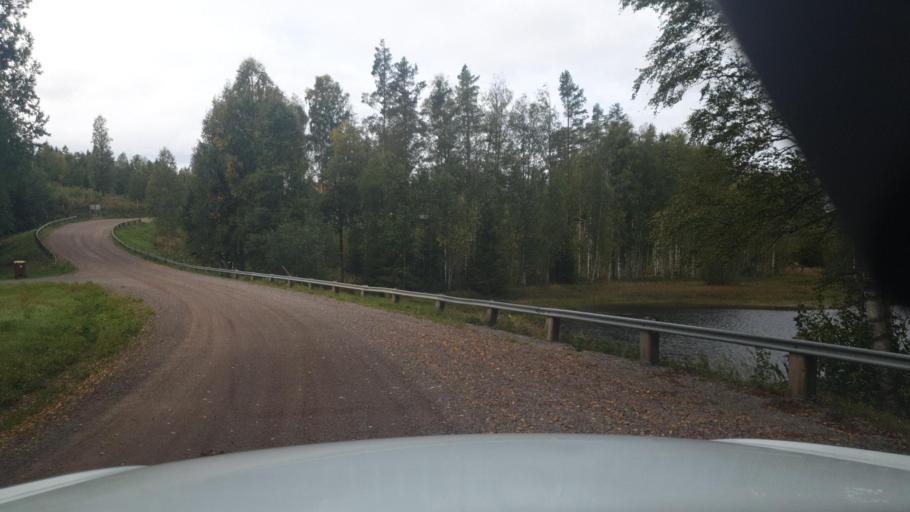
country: SE
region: Vaermland
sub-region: Eda Kommun
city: Charlottenberg
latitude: 60.0891
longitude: 12.5107
